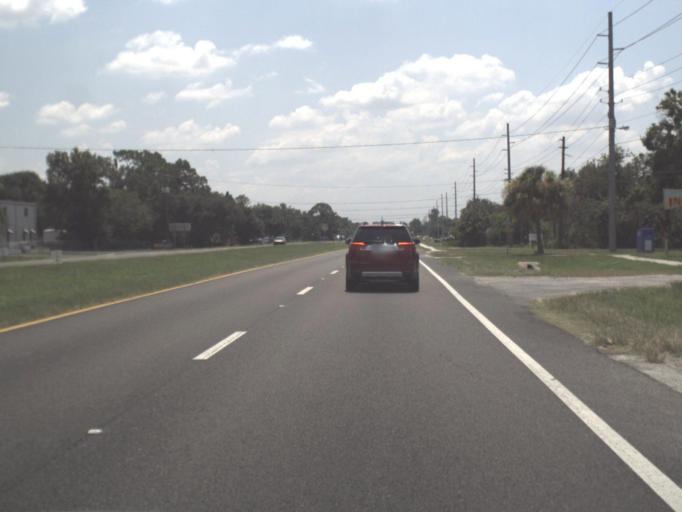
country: US
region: Florida
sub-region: Hillsborough County
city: Gibsonton
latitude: 27.8333
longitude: -82.3818
